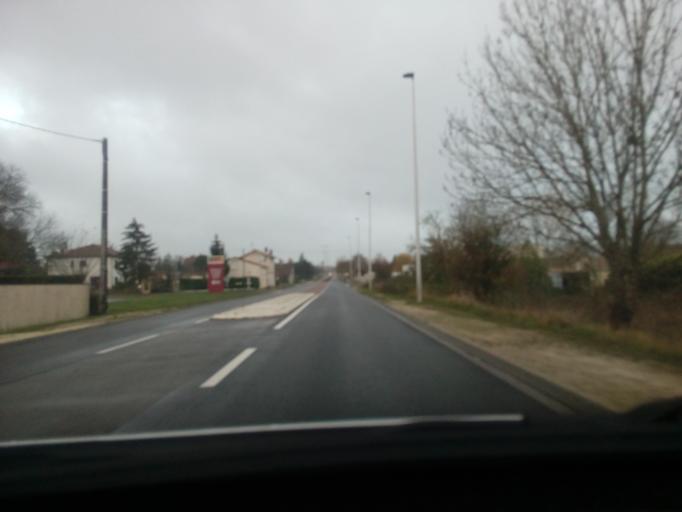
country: FR
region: Poitou-Charentes
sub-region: Departement de la Charente
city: Barbezieux-Saint-Hilaire
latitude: 45.4836
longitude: -0.1408
